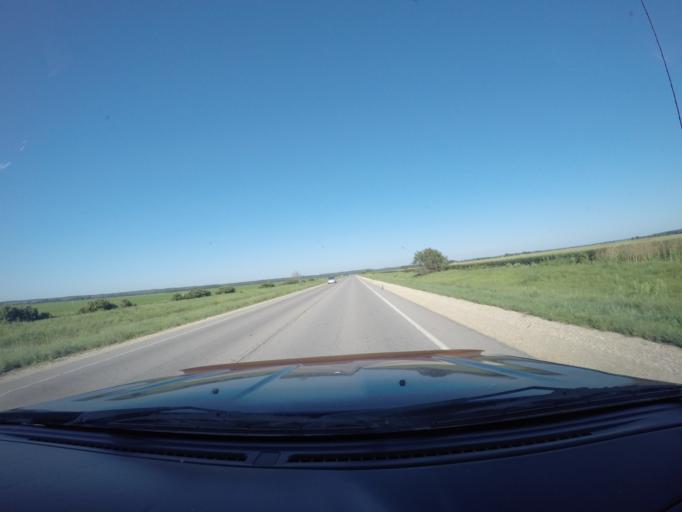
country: US
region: Kansas
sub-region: Jefferson County
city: Oskaloosa
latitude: 39.0872
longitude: -95.4418
